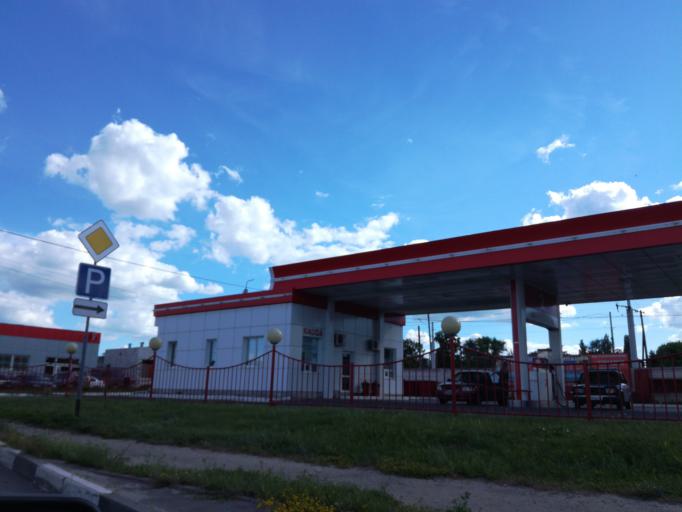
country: RU
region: Kursk
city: Kursk
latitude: 51.7359
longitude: 36.1525
